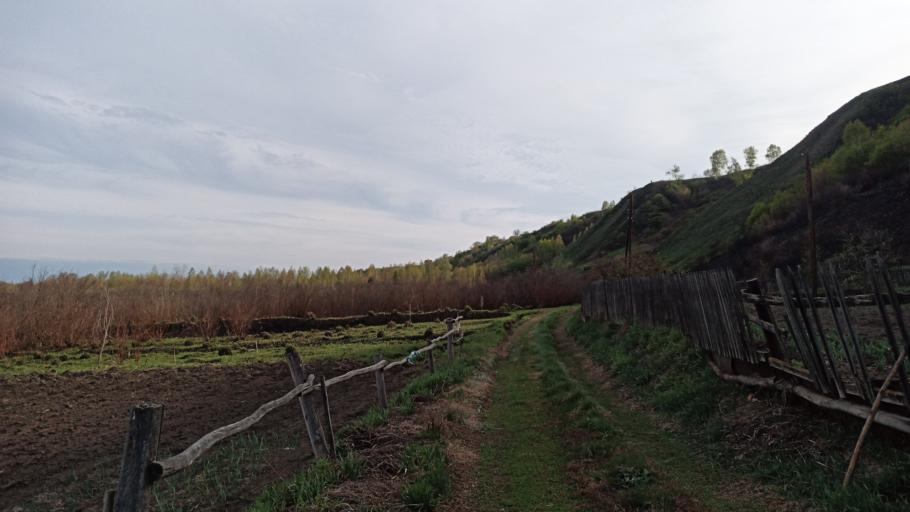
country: RU
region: Altai Krai
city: Yuzhnyy
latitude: 53.2213
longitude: 83.7239
